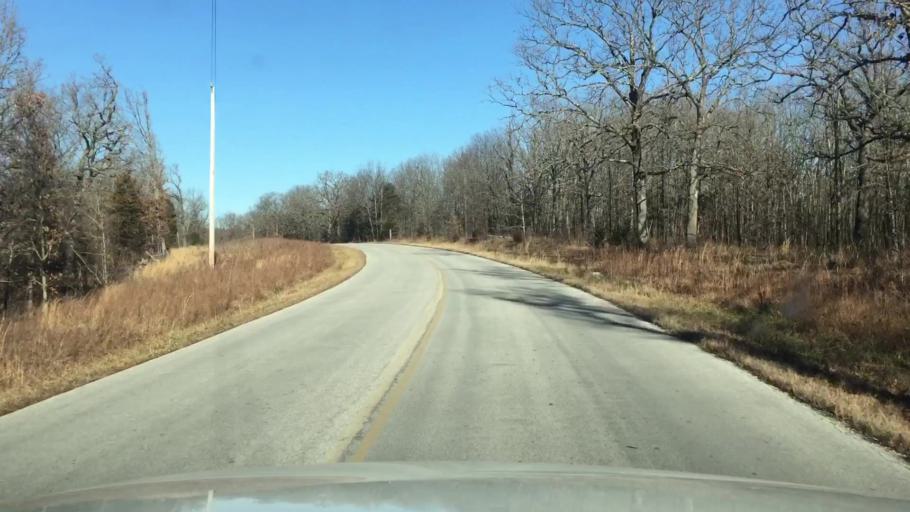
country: US
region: Missouri
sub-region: Morgan County
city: Versailles
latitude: 38.3325
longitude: -92.7694
